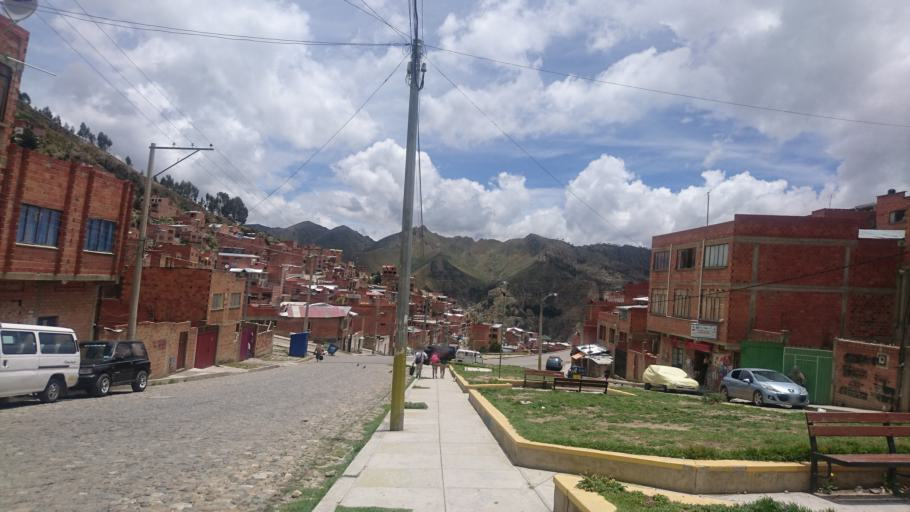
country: BO
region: La Paz
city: La Paz
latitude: -16.4682
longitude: -68.1246
